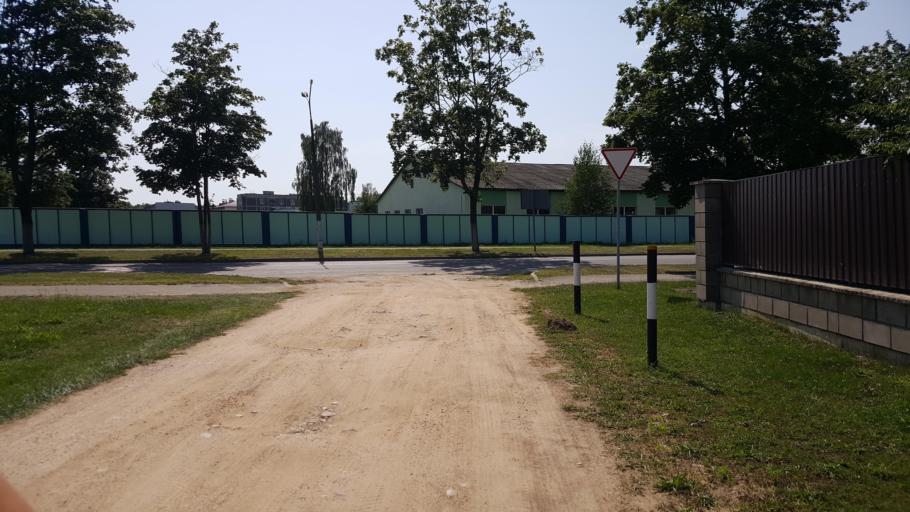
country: BY
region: Brest
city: Zhabinka
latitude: 52.1989
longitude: 24.0308
